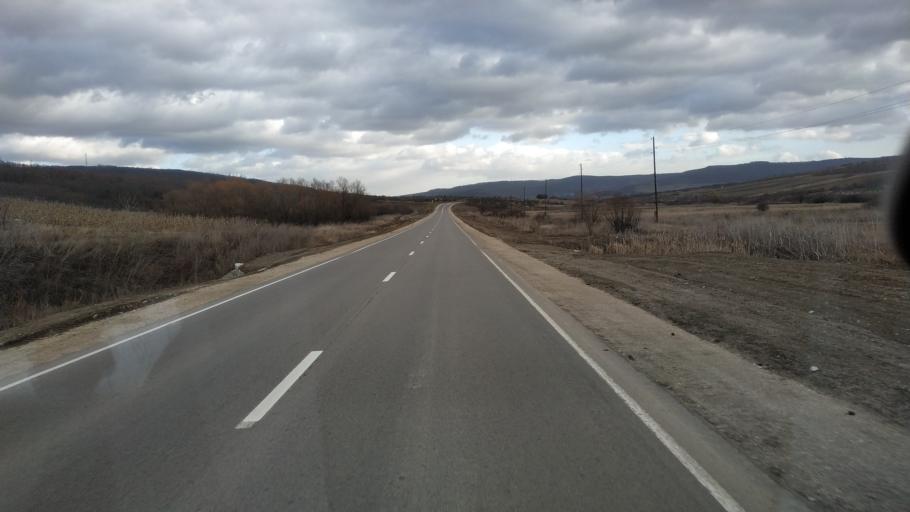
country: MD
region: Calarasi
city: Calarasi
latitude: 47.2731
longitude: 28.2209
